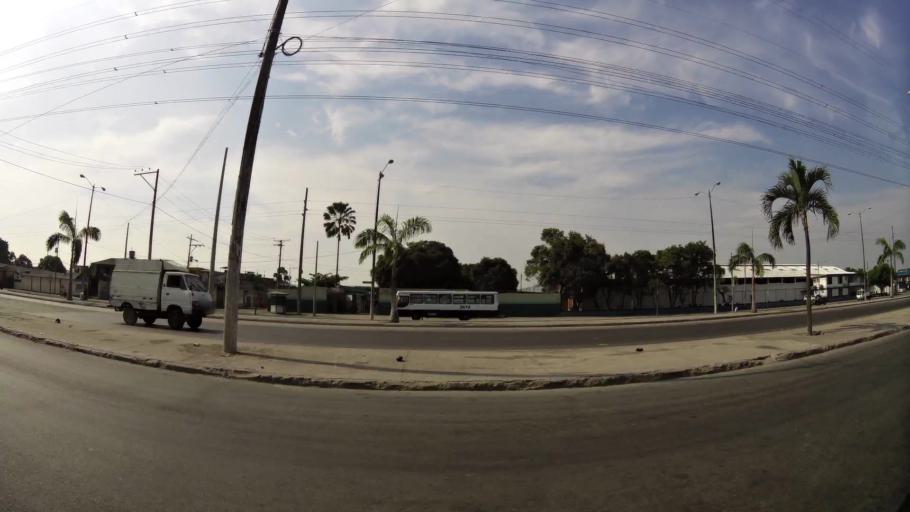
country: EC
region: Guayas
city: Guayaquil
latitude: -2.2618
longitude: -79.8969
